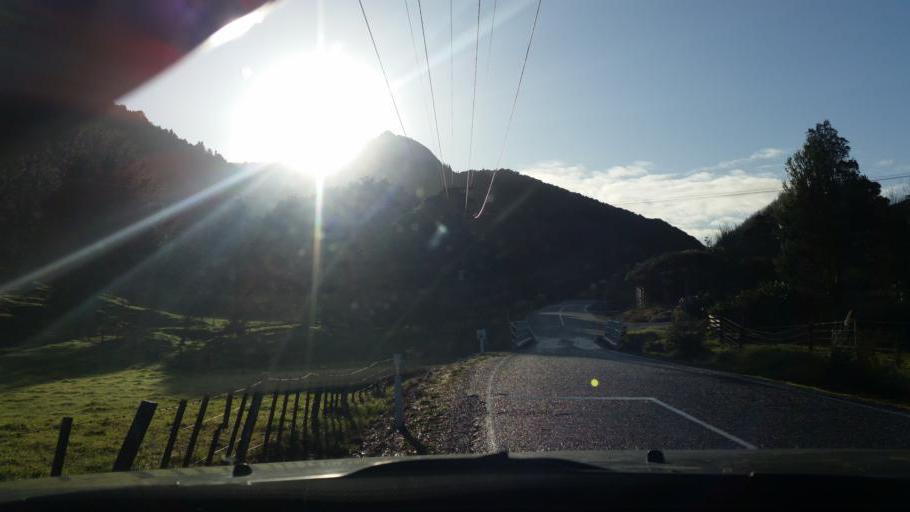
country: NZ
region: Auckland
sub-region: Auckland
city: Wellsford
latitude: -36.1216
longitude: 174.4386
